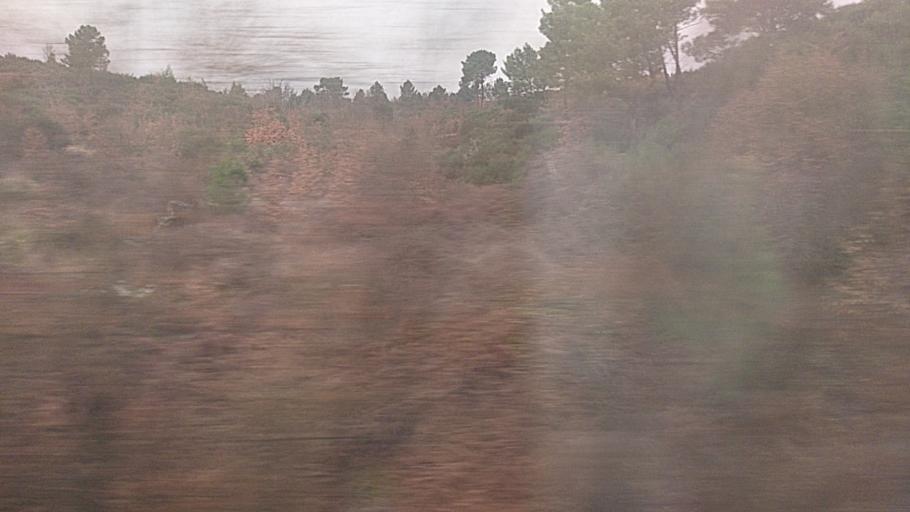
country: PT
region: Guarda
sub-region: Fornos de Algodres
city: Fornos de Algodres
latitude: 40.5988
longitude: -7.5542
